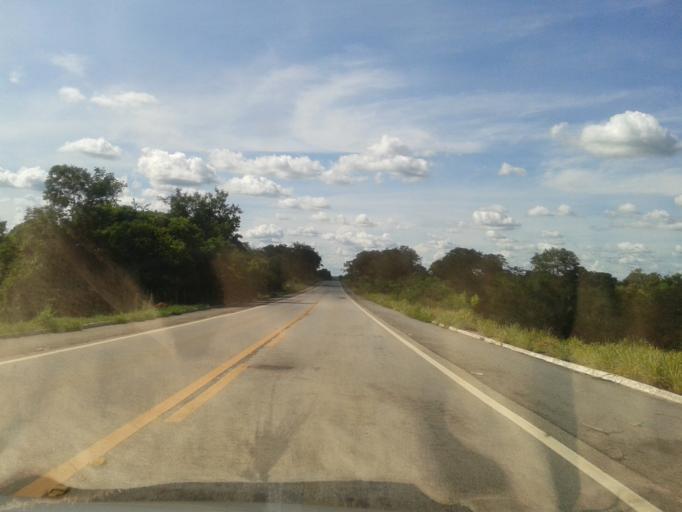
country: BR
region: Goias
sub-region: Mozarlandia
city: Mozarlandia
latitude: -15.2299
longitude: -50.5206
